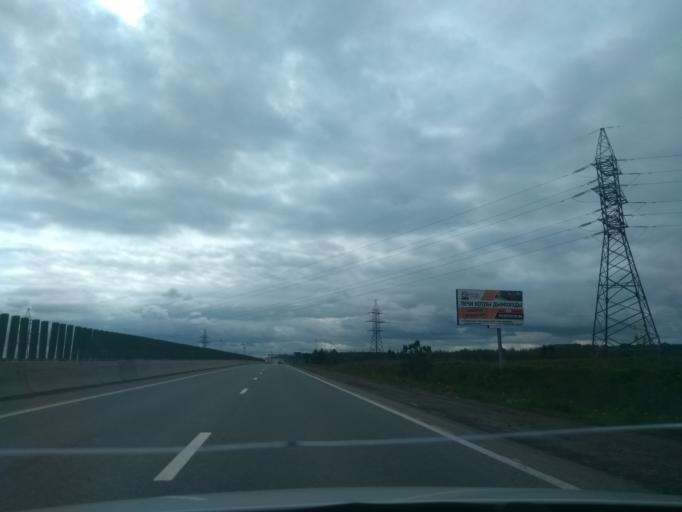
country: RU
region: Perm
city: Froly
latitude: 57.9321
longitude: 56.2827
